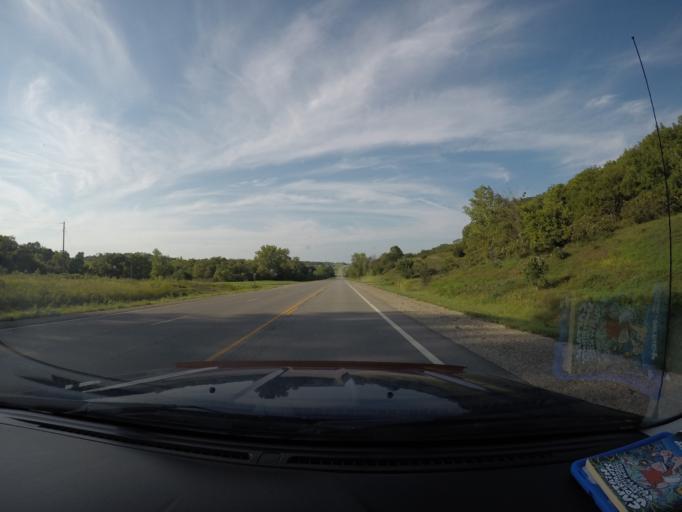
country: US
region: Kansas
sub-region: Atchison County
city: Atchison
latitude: 39.4922
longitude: -95.1315
